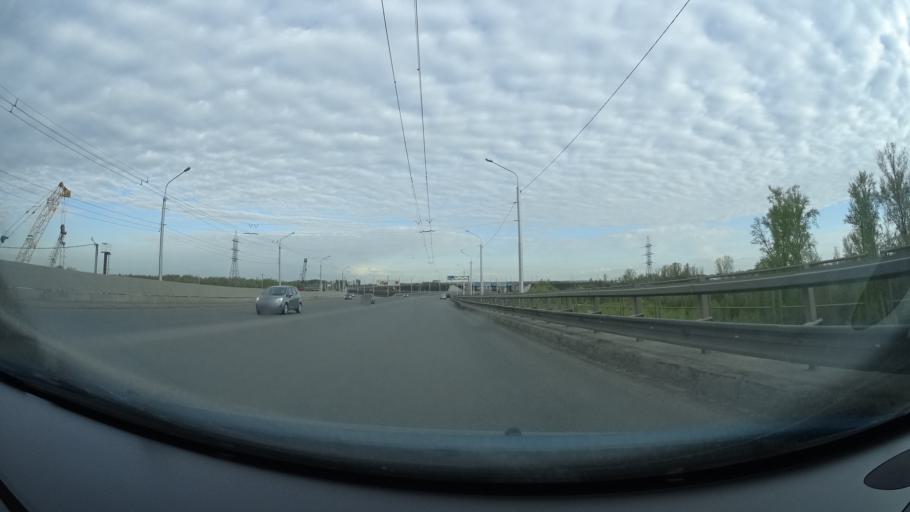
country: RU
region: Bashkortostan
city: Ufa
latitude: 54.7604
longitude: 55.9601
